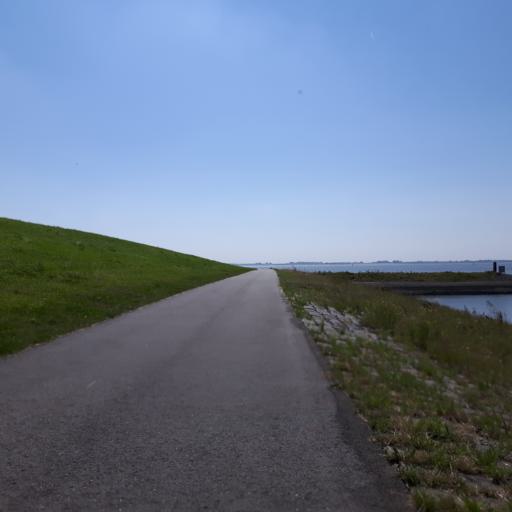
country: NL
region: Zeeland
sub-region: Gemeente Reimerswaal
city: Yerseke
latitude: 51.4338
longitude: 4.0342
